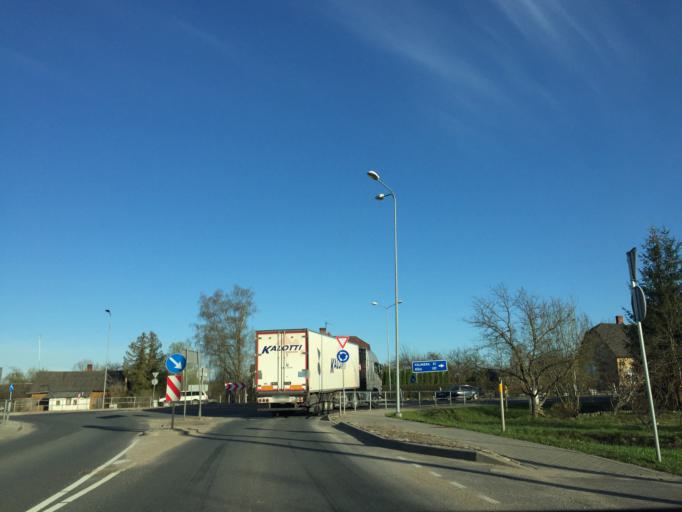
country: LV
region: Valkas Rajons
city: Valka
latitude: 57.7665
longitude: 26.0045
